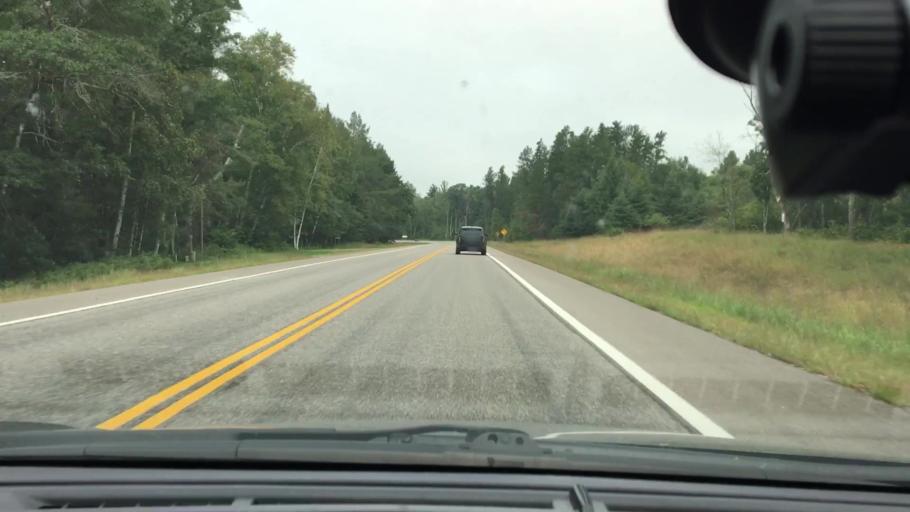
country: US
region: Minnesota
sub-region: Crow Wing County
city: Cross Lake
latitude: 46.6639
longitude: -94.0376
